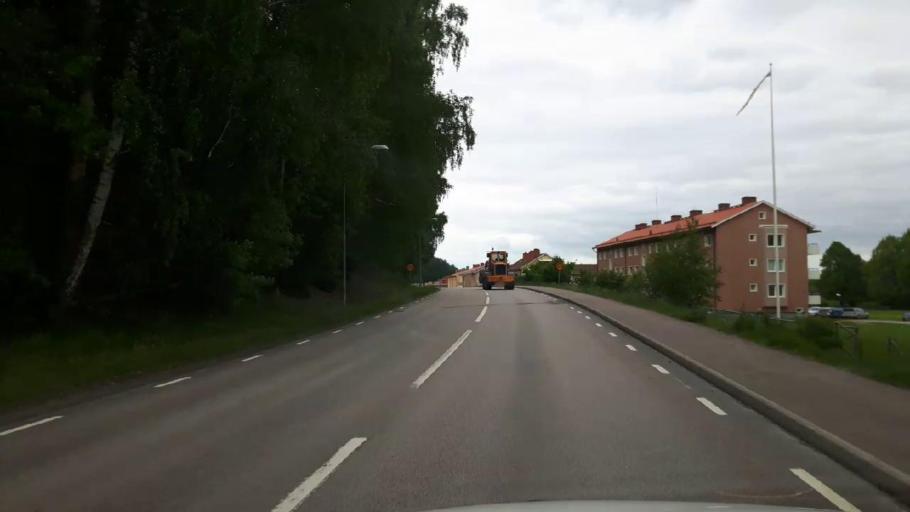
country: SE
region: Vaestmanland
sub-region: Kopings Kommun
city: Kolsva
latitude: 59.6042
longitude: 15.8347
